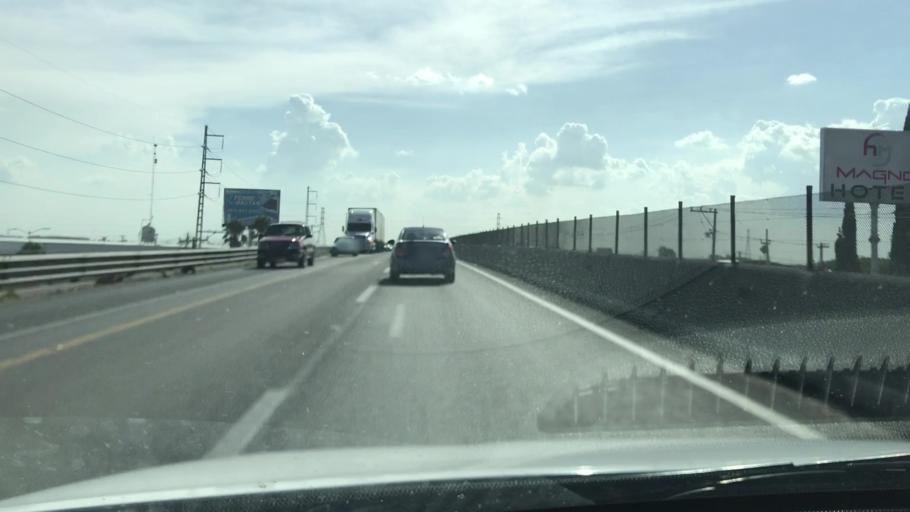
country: MX
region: Guanajuato
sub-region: Celaya
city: Colonia Fraccionamiento el Puente
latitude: 20.5155
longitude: -100.8936
